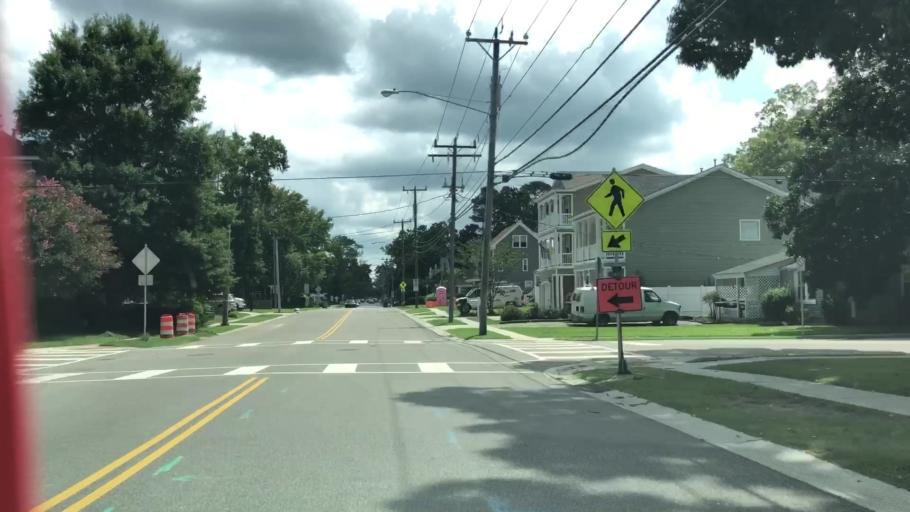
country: US
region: Virginia
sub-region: City of Virginia Beach
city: Virginia Beach
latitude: 36.8407
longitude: -75.9802
